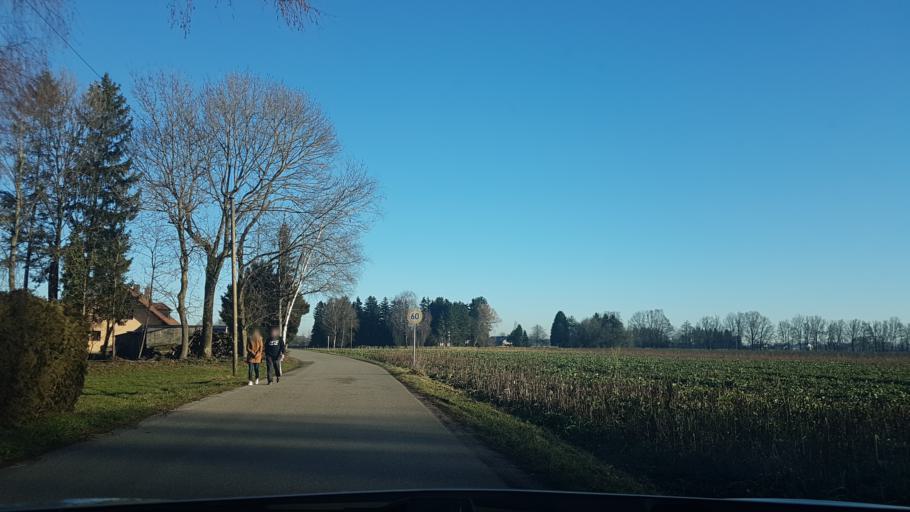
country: DE
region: Bavaria
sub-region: Upper Bavaria
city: Eichenried
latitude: 48.2874
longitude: 11.7974
